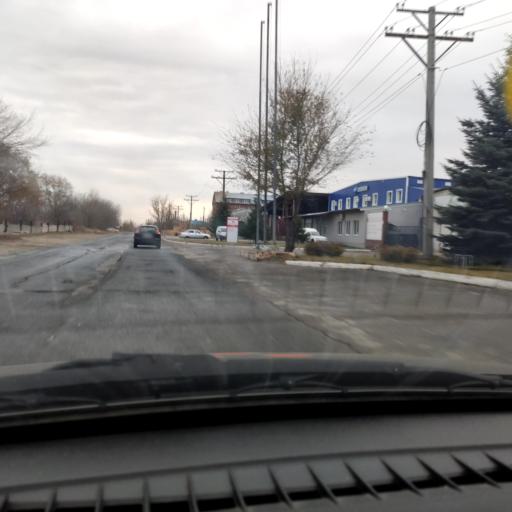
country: RU
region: Samara
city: Tol'yatti
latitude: 53.5536
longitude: 49.3243
